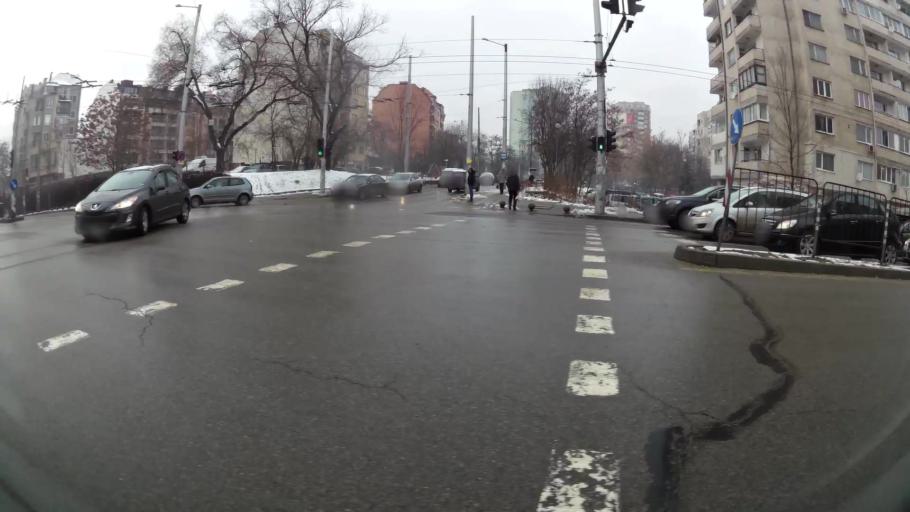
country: BG
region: Sofia-Capital
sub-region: Stolichna Obshtina
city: Sofia
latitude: 42.7084
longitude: 23.3133
